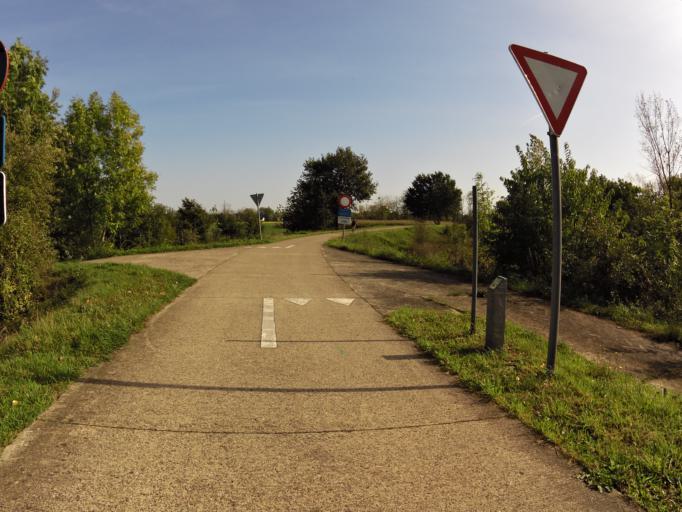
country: NL
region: Limburg
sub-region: Gemeente Stein
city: Stein
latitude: 50.9840
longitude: 5.7320
